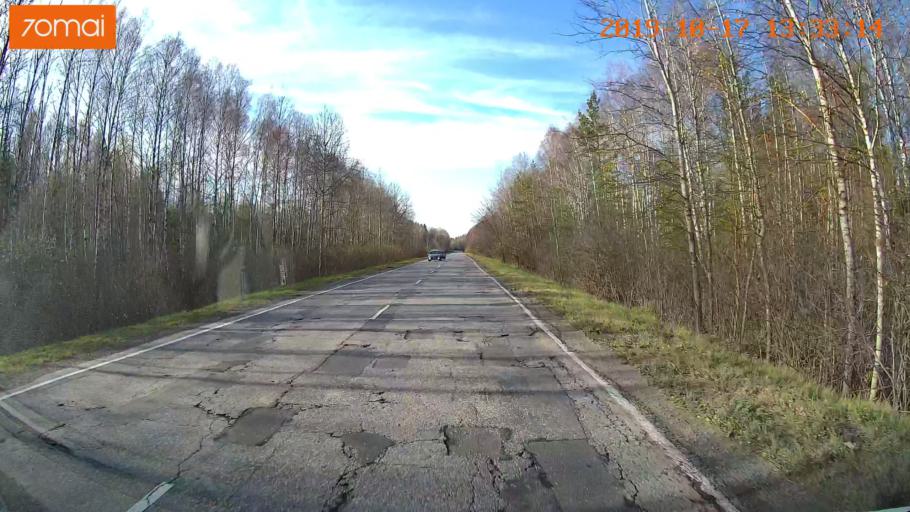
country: RU
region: Vladimir
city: Velikodvorskiy
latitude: 55.1414
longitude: 40.7462
